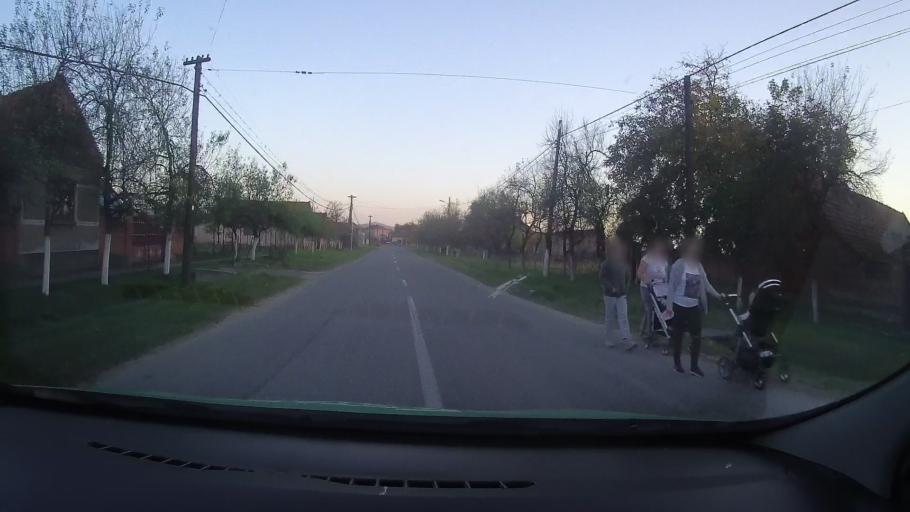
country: RO
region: Timis
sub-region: Comuna Manastiur
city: Manastiur
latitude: 45.8325
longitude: 22.0656
